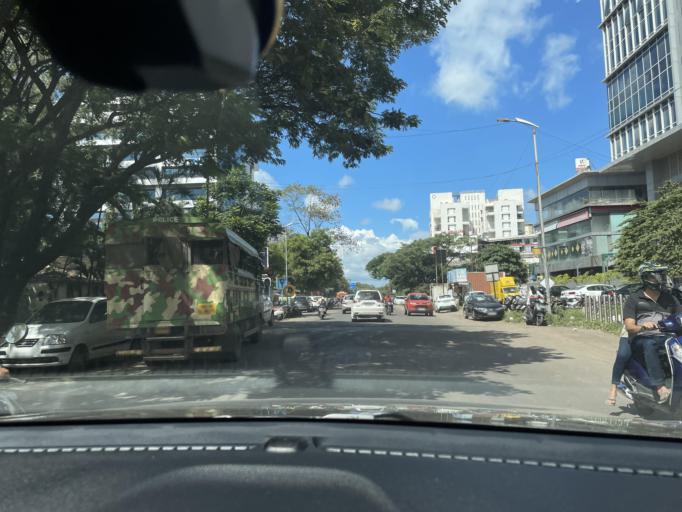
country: IN
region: Maharashtra
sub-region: Pune Division
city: Shivaji Nagar
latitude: 18.5221
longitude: 73.7796
